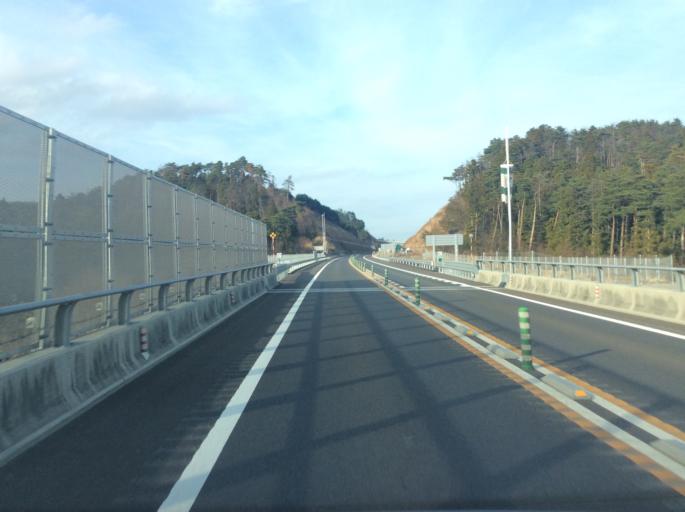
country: JP
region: Fukushima
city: Namie
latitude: 37.4349
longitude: 140.9588
